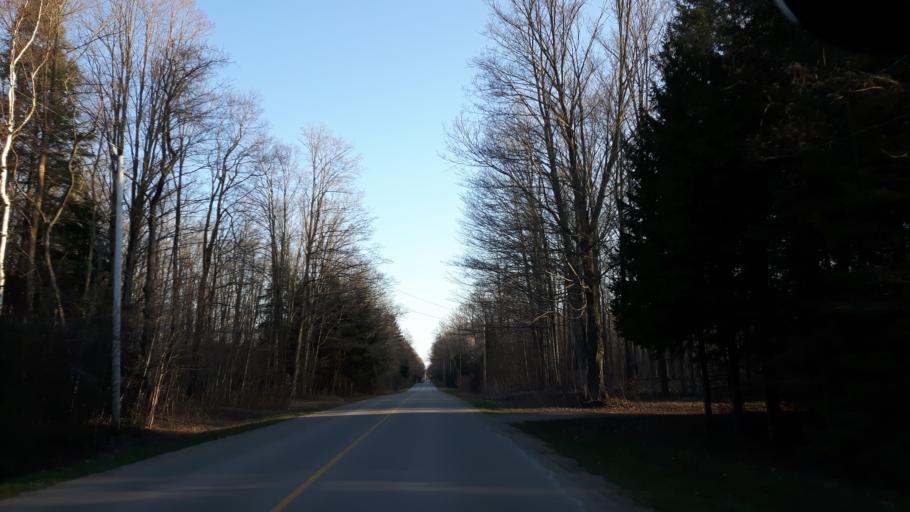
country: CA
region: Ontario
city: Goderich
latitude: 43.5987
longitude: -81.6849
